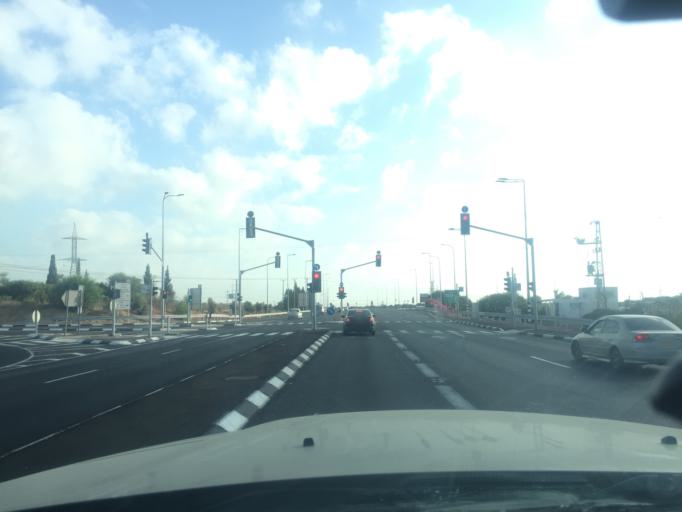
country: PS
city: Umm an Nasr
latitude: 31.6020
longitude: 34.5713
